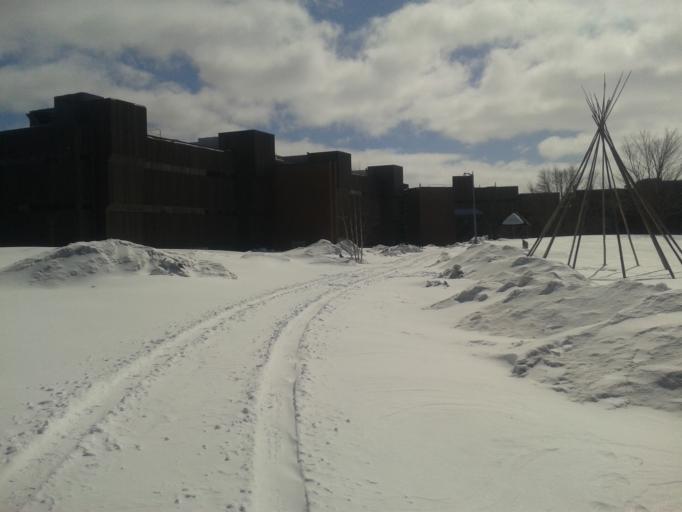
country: CA
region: Ontario
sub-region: Nipissing District
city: North Bay
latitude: 46.3446
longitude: -79.4936
